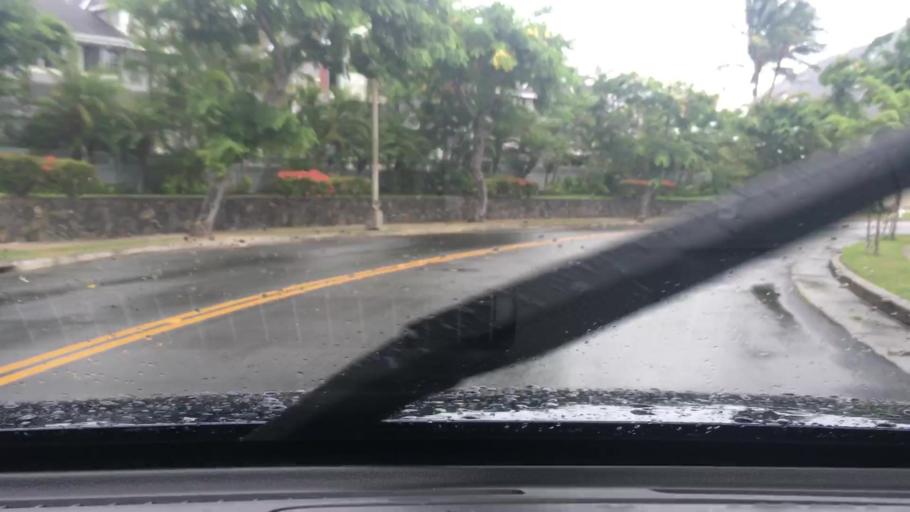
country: US
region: Hawaii
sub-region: Honolulu County
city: Waimanalo Beach
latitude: 21.2898
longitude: -157.7018
